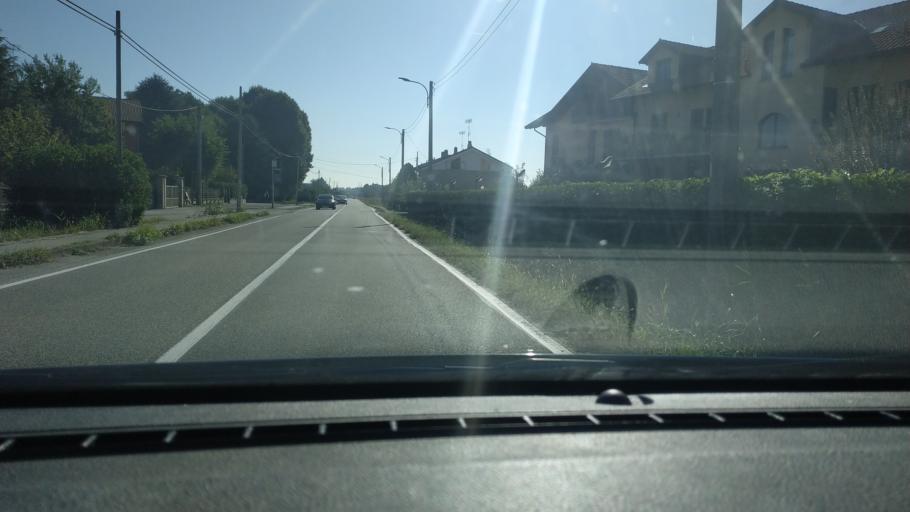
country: IT
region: Piedmont
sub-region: Provincia di Torino
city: Verolengo
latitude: 45.1976
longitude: 7.9372
